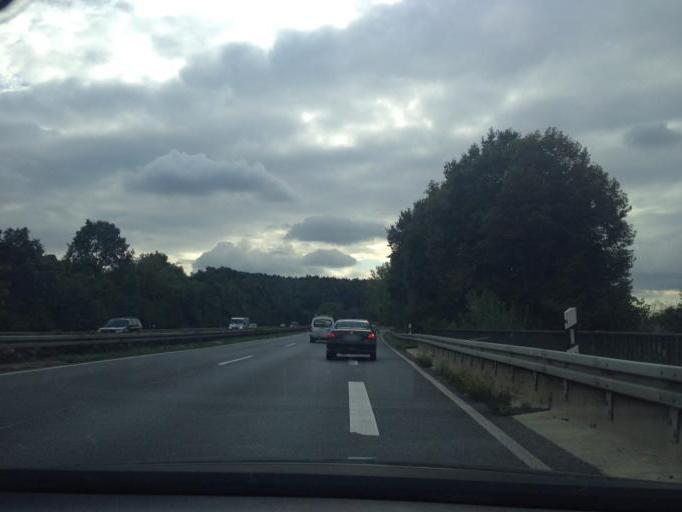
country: DE
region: Hesse
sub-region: Regierungsbezirk Giessen
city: Wetzlar
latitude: 50.5679
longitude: 8.5250
